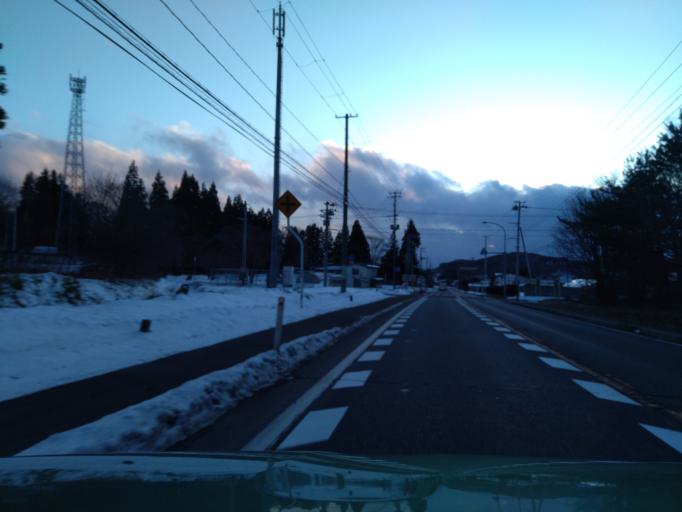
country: JP
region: Iwate
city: Shizukuishi
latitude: 39.6954
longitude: 141.0191
